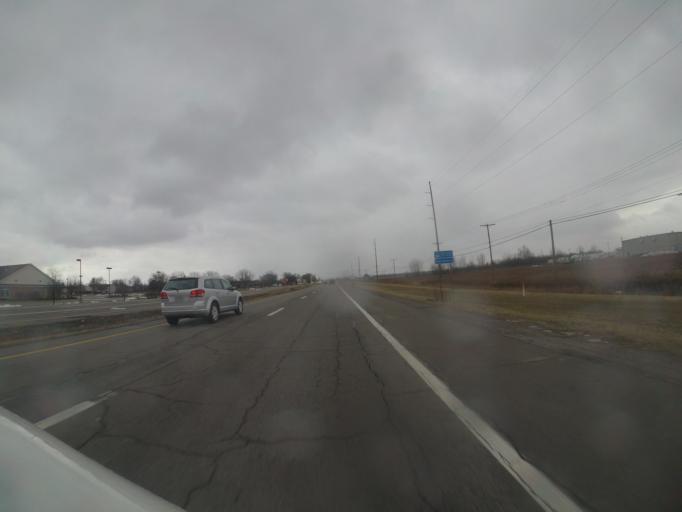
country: US
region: Ohio
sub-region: Wood County
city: Walbridge
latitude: 41.5639
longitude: -83.5371
